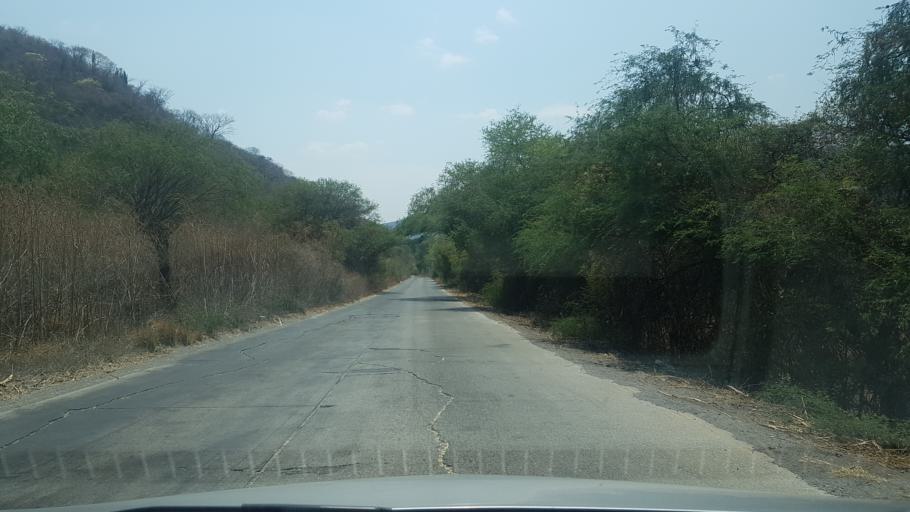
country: MX
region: Morelos
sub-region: Tlaltizapan de Zapata
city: Colonia Palo Prieto (Chipitongo)
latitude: 18.7563
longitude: -99.1101
